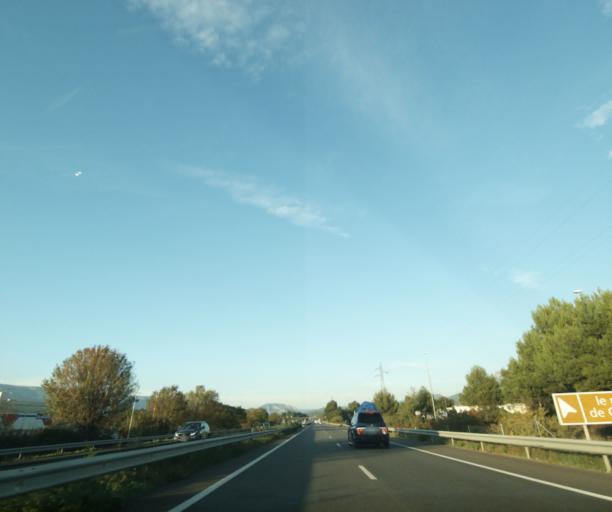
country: FR
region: Provence-Alpes-Cote d'Azur
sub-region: Departement des Bouches-du-Rhone
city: Aubagne
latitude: 43.2915
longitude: 5.5873
